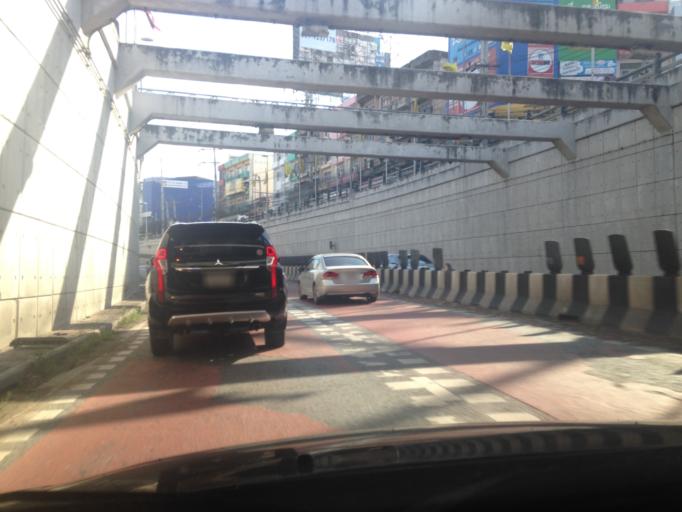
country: TH
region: Nonthaburi
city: Pak Kret
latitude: 13.9075
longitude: 100.5044
